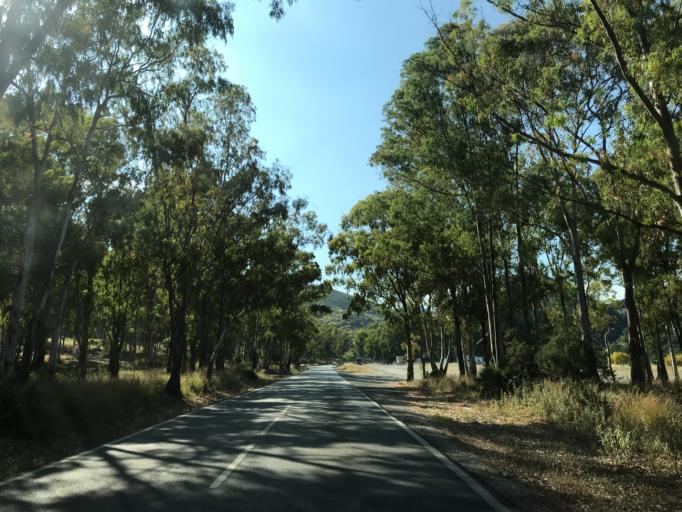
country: ES
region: Andalusia
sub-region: Provincia de Malaga
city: Benahavis
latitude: 36.5060
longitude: -5.0307
